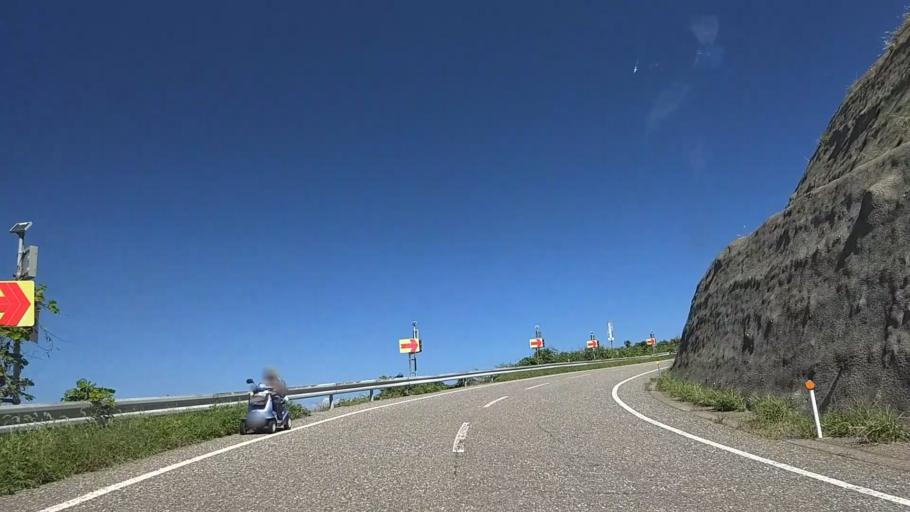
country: JP
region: Niigata
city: Joetsu
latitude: 37.1714
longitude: 138.0957
